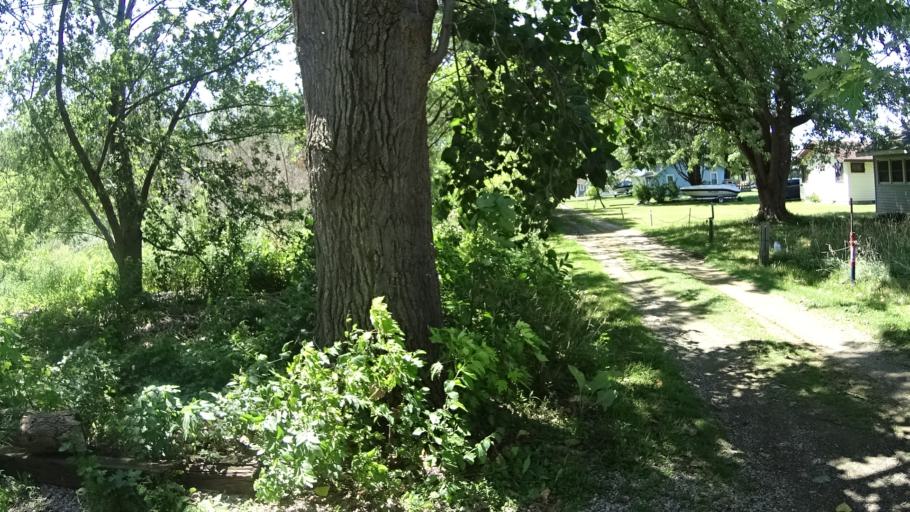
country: US
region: Ohio
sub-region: Ottawa County
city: Port Clinton
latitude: 41.4370
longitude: -82.8881
